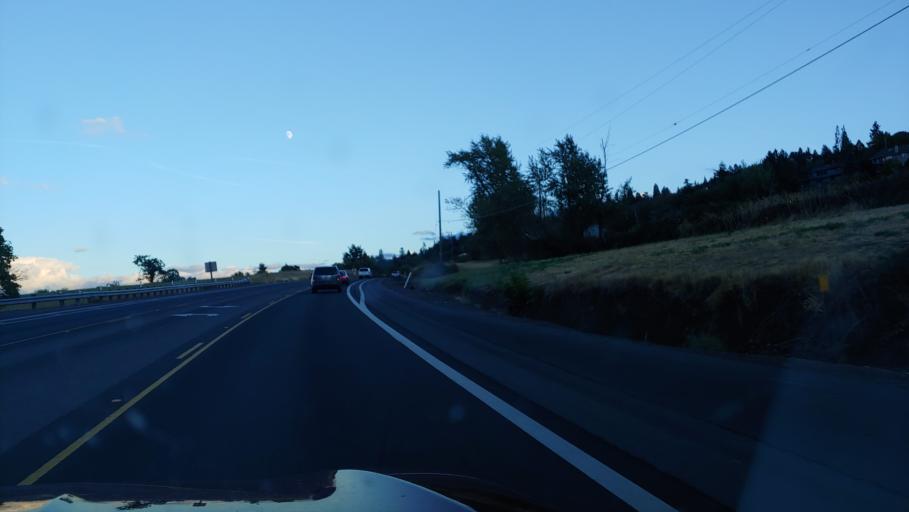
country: US
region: Oregon
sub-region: Jackson County
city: Ashland
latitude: 42.2165
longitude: -122.7332
